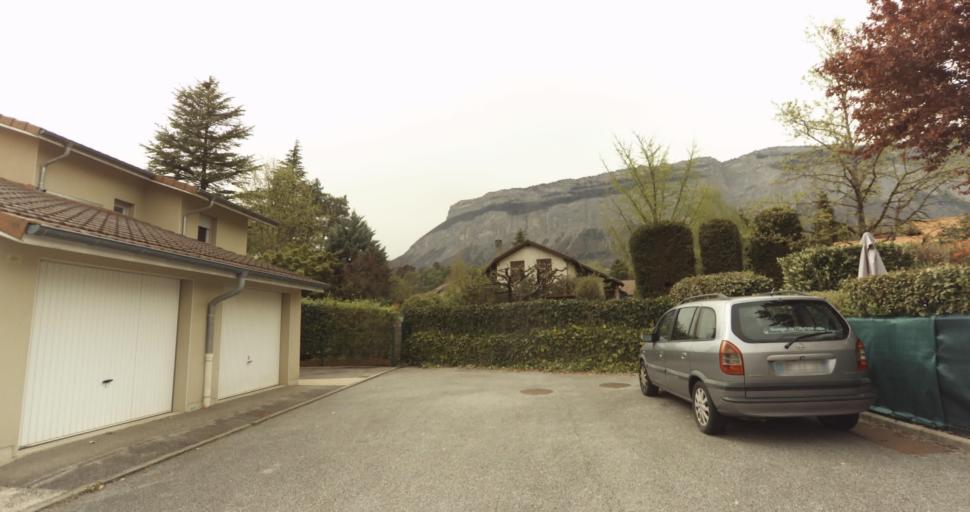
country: FR
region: Rhone-Alpes
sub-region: Departement de l'Isere
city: Montbonnot-Saint-Martin
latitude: 45.2231
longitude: 5.8117
